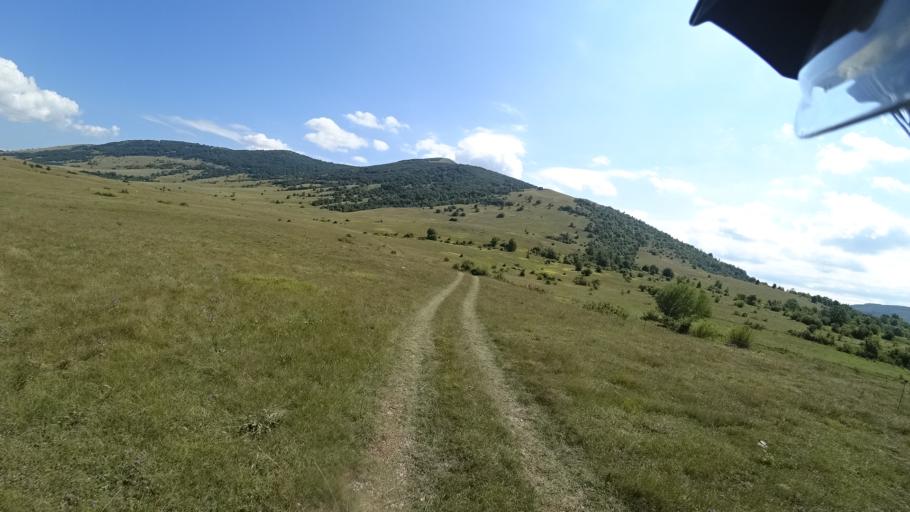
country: HR
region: Zadarska
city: Gracac
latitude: 44.4005
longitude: 15.9167
